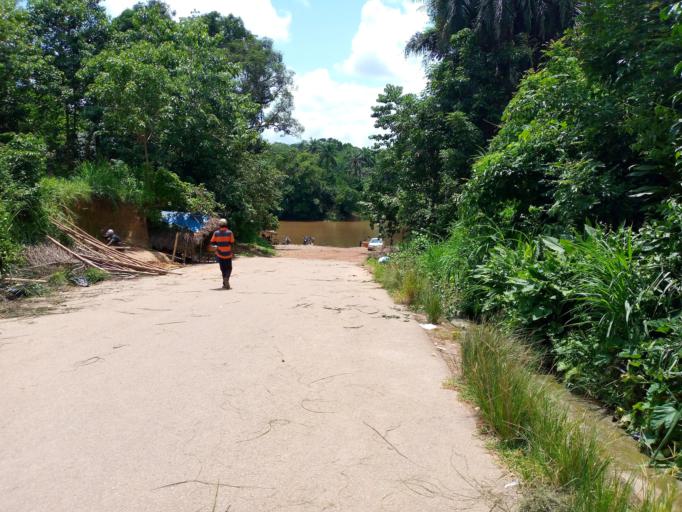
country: SL
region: Northern Province
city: Magburaka
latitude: 8.7247
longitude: -11.9528
